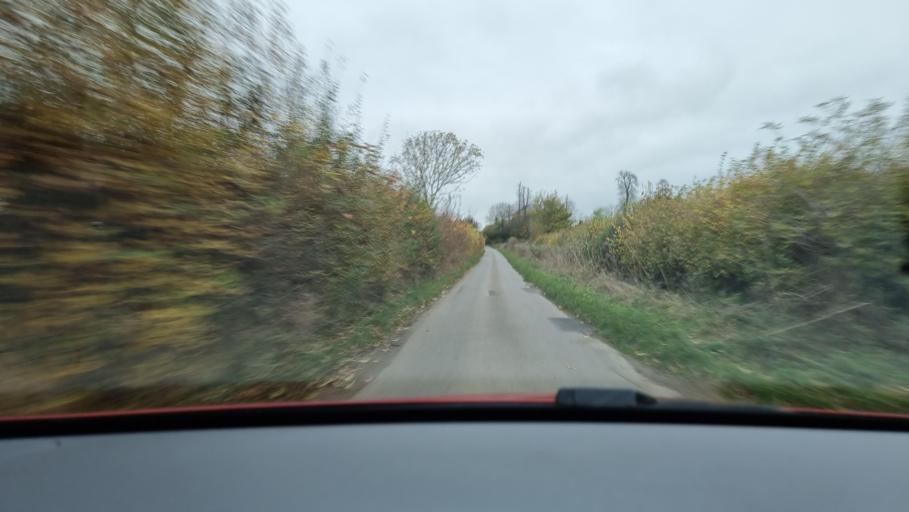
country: GB
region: England
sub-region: Oxfordshire
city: Woodstock
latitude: 51.8720
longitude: -1.3098
